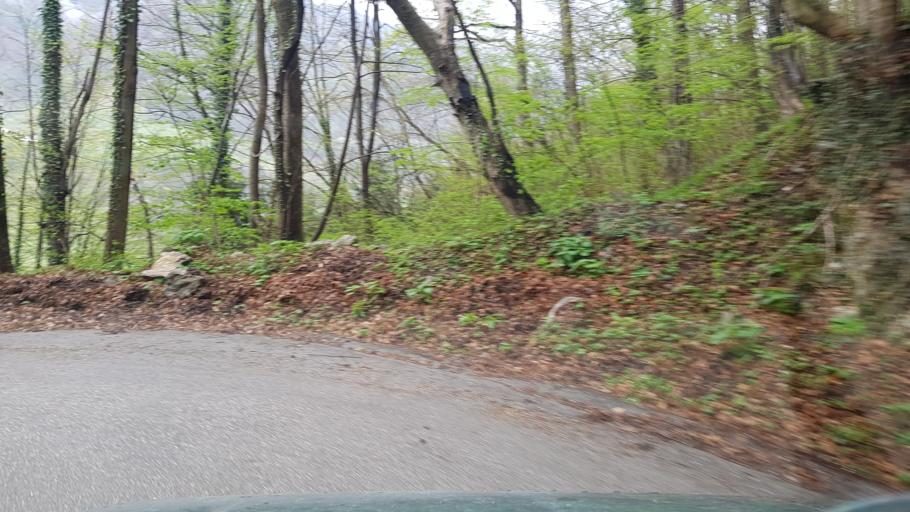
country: SI
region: Tolmin
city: Tolmin
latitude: 46.1431
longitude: 13.7774
